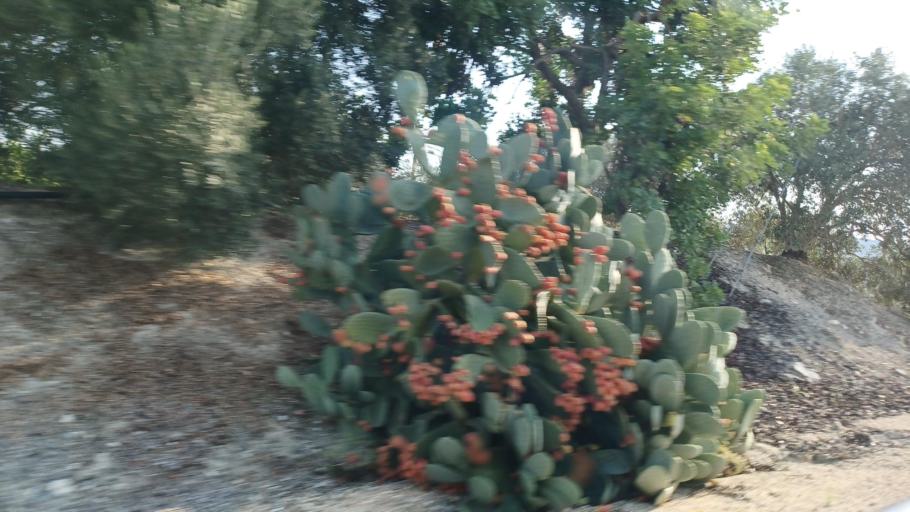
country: CY
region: Pafos
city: Polis
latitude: 34.9816
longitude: 32.4728
